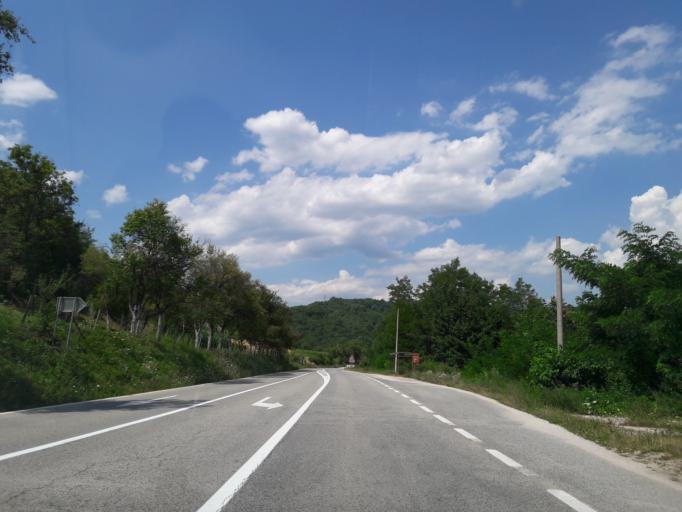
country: BA
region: Republika Srpska
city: Mrkonjic Grad
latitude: 44.5359
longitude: 17.1494
